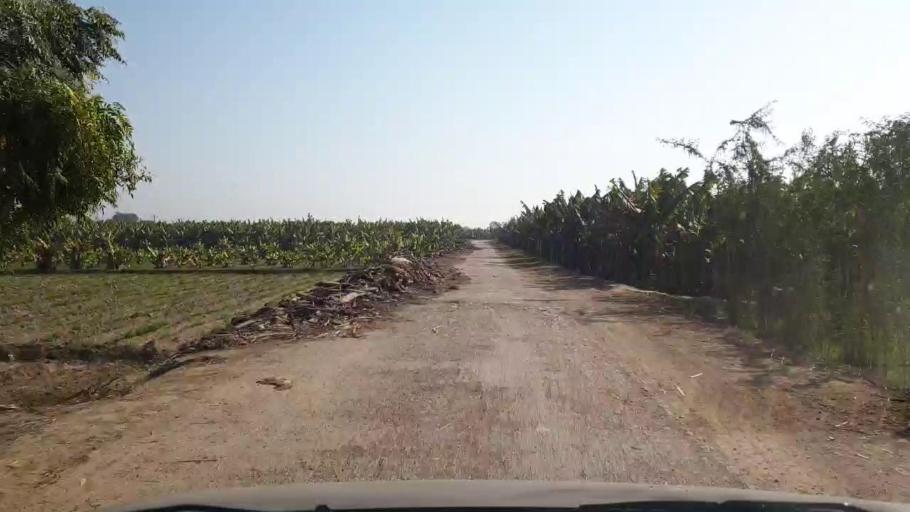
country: PK
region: Sindh
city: Tando Jam
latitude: 25.4358
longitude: 68.6122
